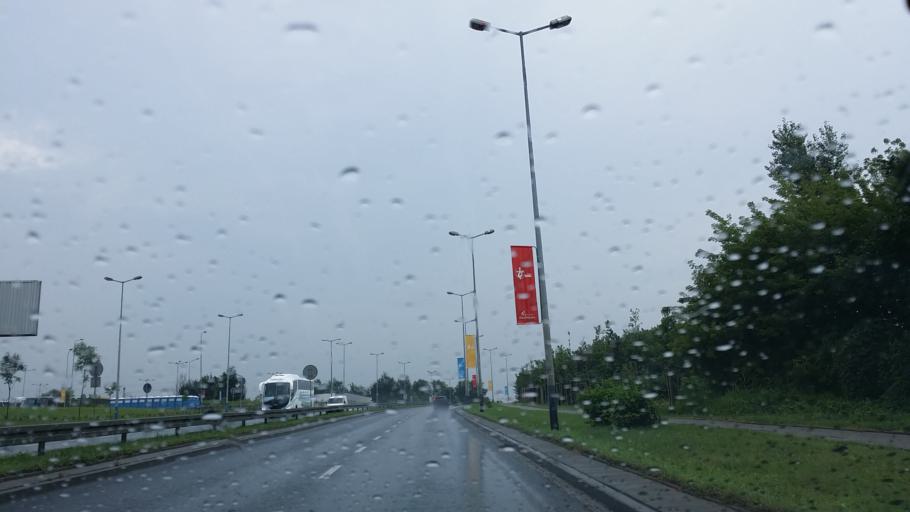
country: PL
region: Lesser Poland Voivodeship
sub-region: Krakow
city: Krakow
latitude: 50.0244
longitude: 19.9455
